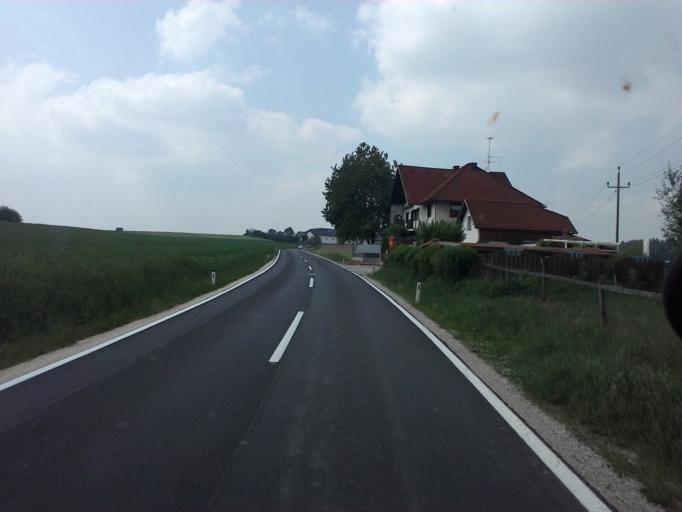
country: AT
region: Upper Austria
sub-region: Wels-Land
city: Sattledt
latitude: 48.0695
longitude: 14.0821
